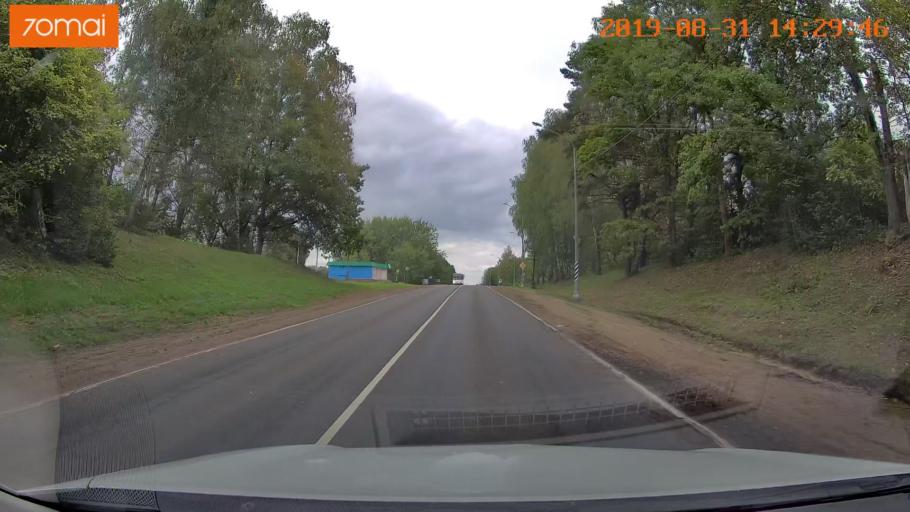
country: RU
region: Smolensk
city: Yekimovichi
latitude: 54.1278
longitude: 33.3385
